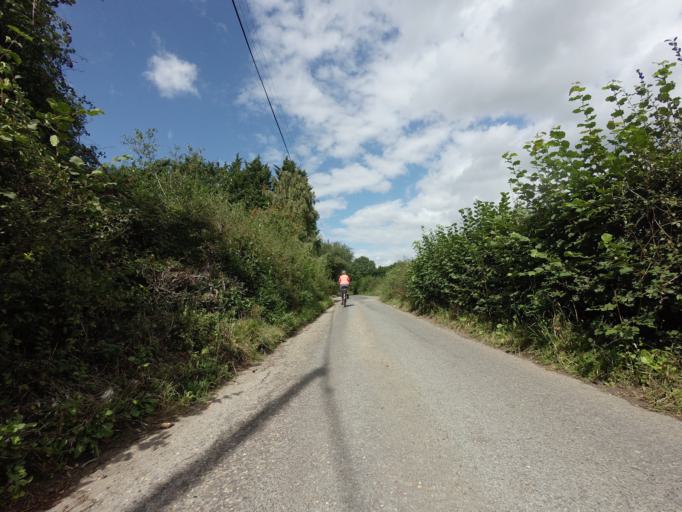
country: GB
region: England
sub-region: Kent
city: Shoreham
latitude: 51.3069
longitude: 0.1797
